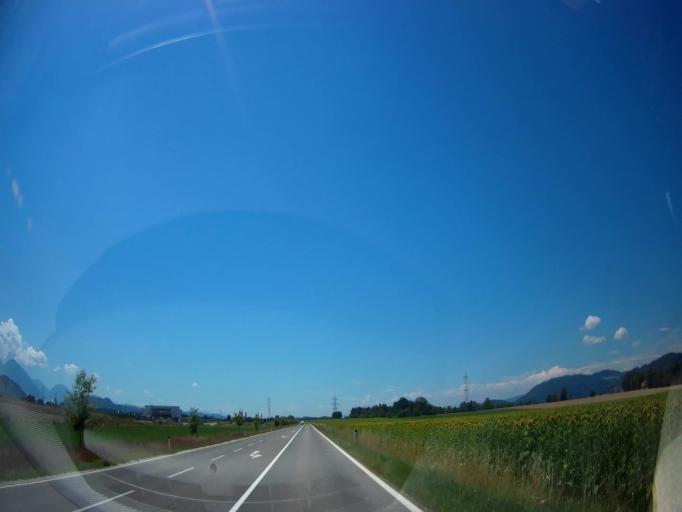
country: AT
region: Carinthia
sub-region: Politischer Bezirk Volkermarkt
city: Voelkermarkt
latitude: 46.6264
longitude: 14.6266
